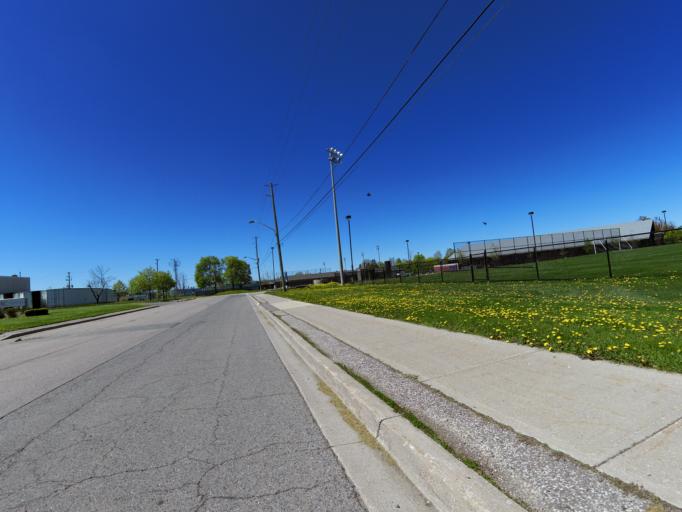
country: CA
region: Ontario
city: Brampton
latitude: 43.7053
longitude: -79.6976
